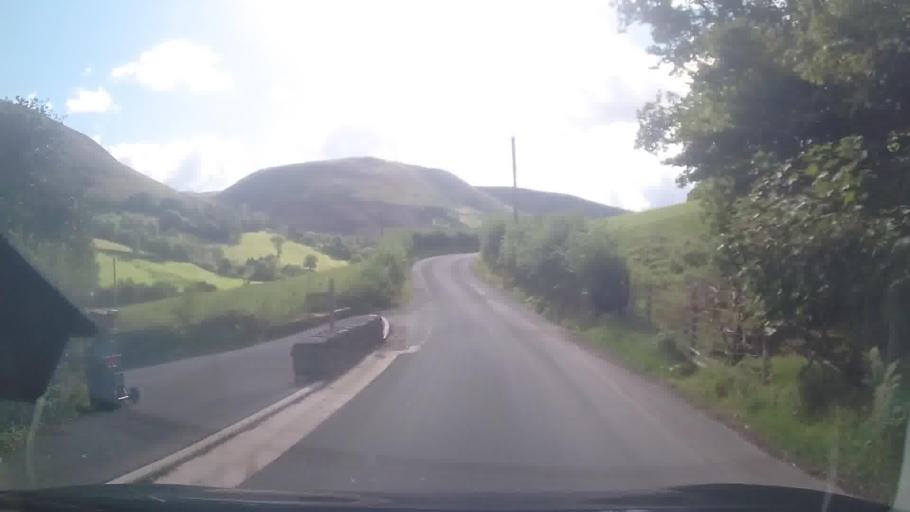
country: GB
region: Wales
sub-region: Gwynedd
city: Bala
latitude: 52.7408
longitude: -3.6431
